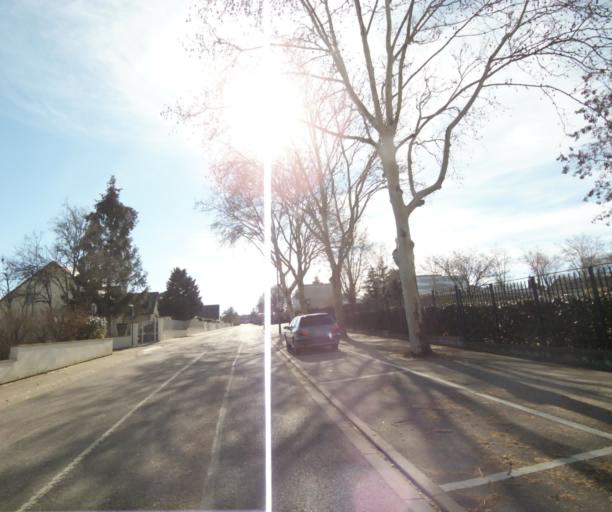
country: FR
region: Lorraine
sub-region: Departement de Meurthe-et-Moselle
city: Villers-les-Nancy
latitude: 48.6660
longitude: 6.1406
